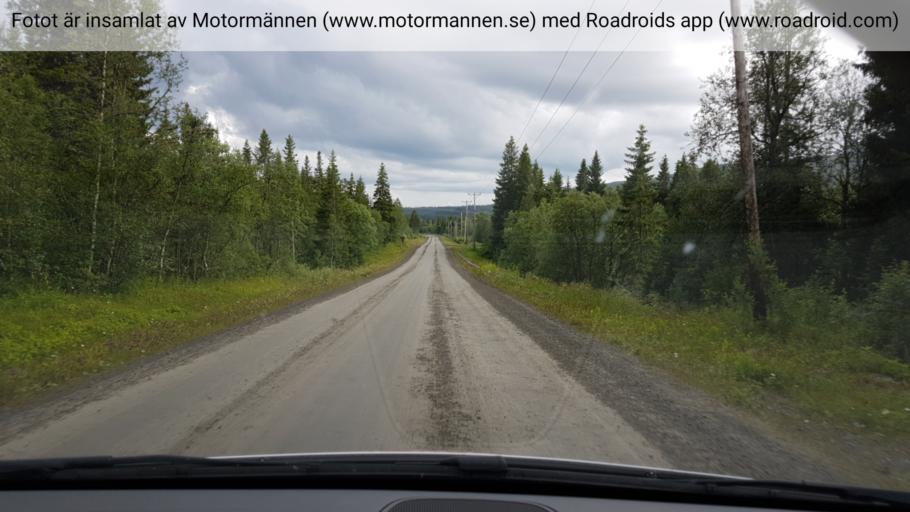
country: SE
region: Jaemtland
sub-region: Are Kommun
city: Are
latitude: 63.6837
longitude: 12.8084
